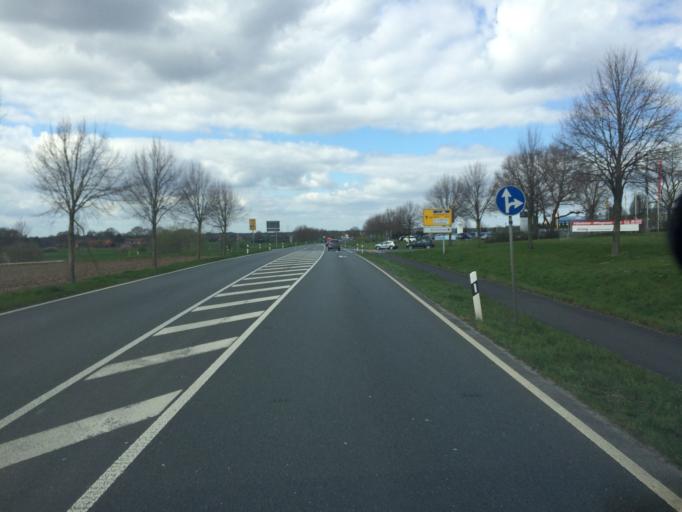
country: DE
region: North Rhine-Westphalia
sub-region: Regierungsbezirk Munster
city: Coesfeld
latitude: 51.9222
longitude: 7.1610
